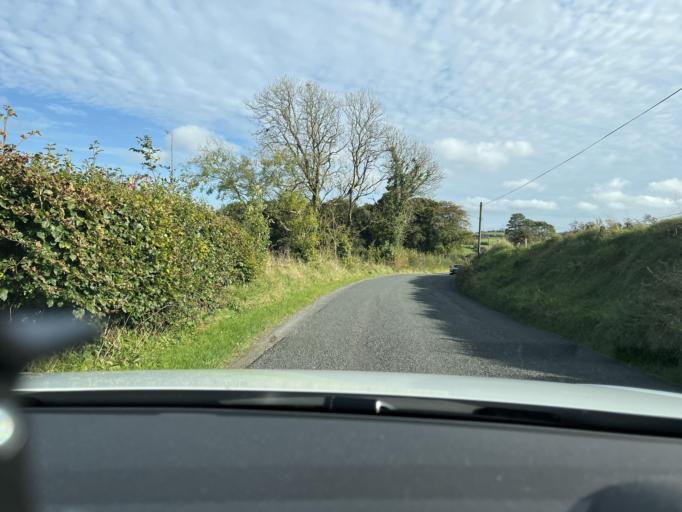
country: IE
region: Connaught
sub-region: Sligo
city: Ballymote
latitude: 54.0769
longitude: -8.4007
